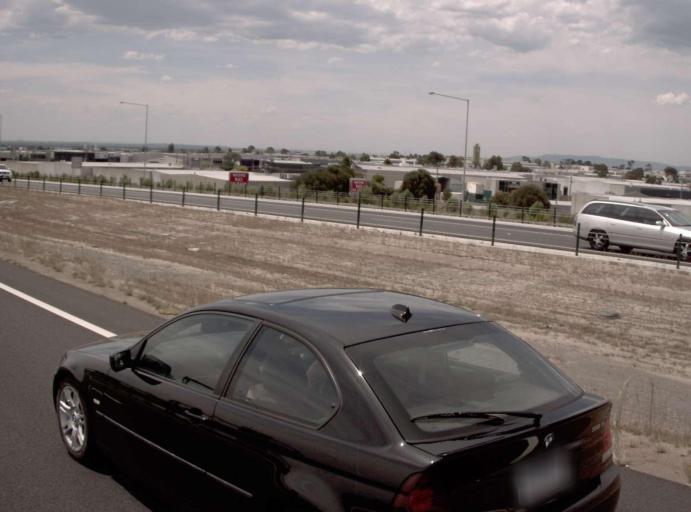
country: AU
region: Victoria
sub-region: Frankston
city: Carrum Downs
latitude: -38.1076
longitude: 145.1609
